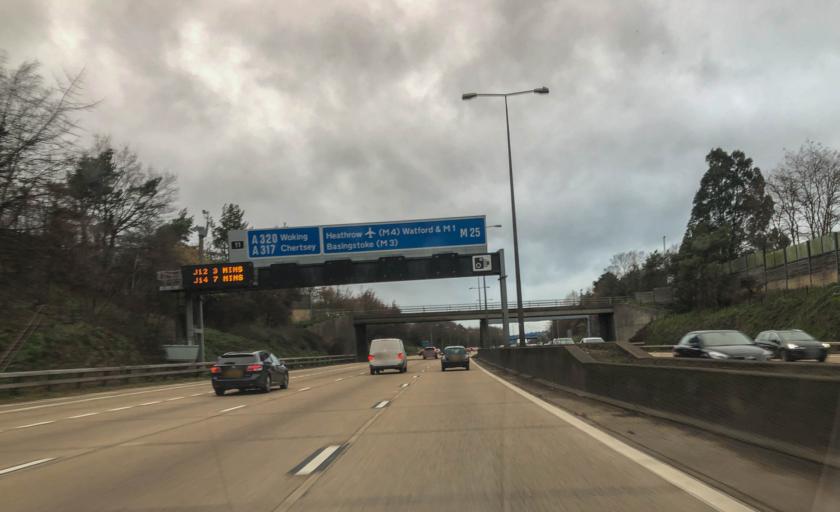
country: GB
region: England
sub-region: Surrey
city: Addlestone
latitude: 51.3667
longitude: -0.5040
